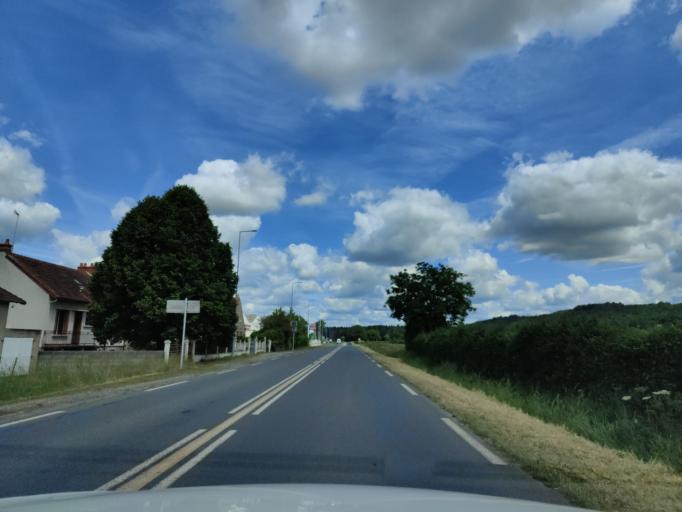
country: FR
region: Auvergne
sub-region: Departement de l'Allier
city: Estivareilles
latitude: 46.4275
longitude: 2.6135
